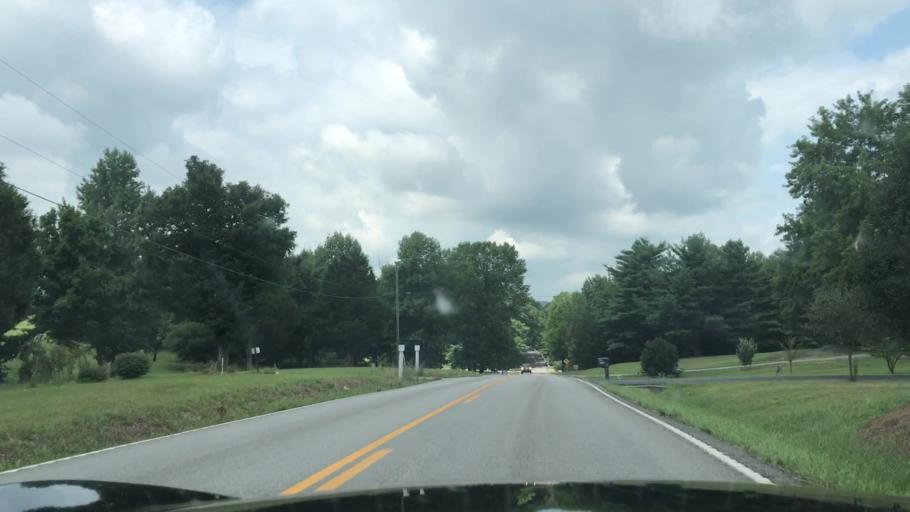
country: US
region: Kentucky
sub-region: Muhlenberg County
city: Greenville
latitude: 37.2027
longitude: -87.0965
